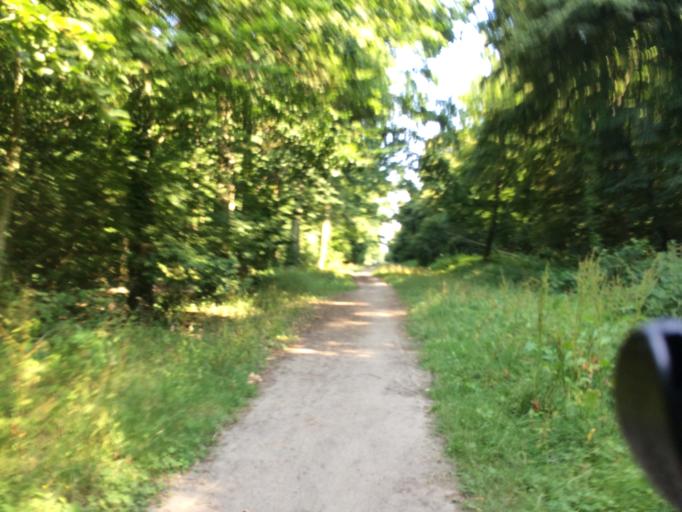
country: FR
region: Ile-de-France
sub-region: Departement de l'Essonne
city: Montgeron
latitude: 48.6843
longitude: 2.4429
